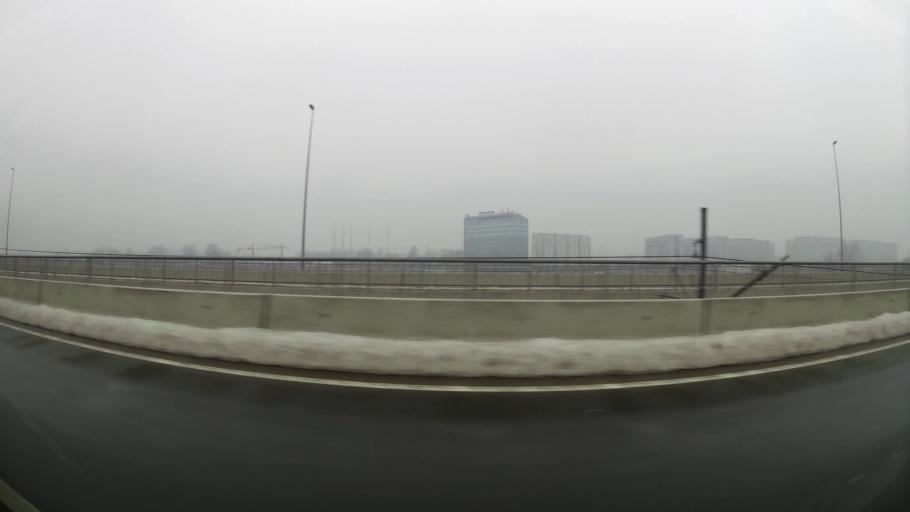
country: RS
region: Central Serbia
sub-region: Belgrade
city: Novi Beograd
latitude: 44.8075
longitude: 20.4150
